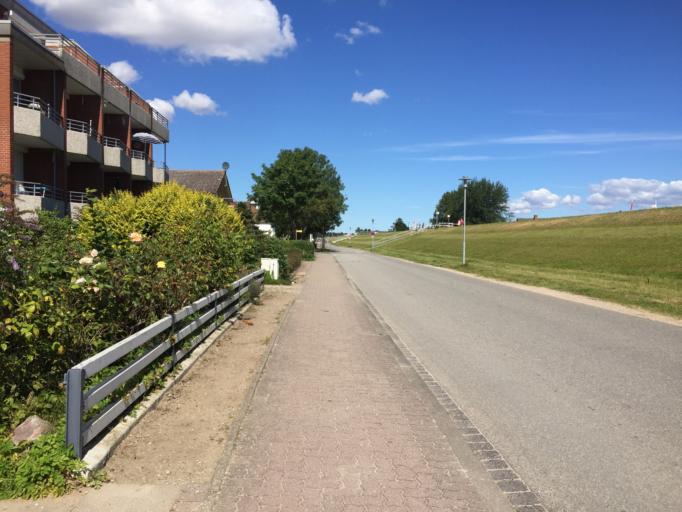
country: DE
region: Schleswig-Holstein
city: Dahme
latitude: 54.2234
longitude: 11.0869
